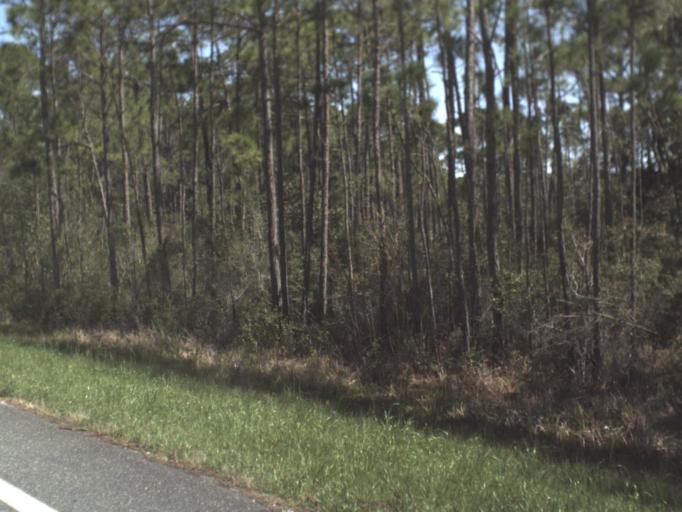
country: US
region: Florida
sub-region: Wakulla County
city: Crawfordville
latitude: 30.0020
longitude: -84.3977
